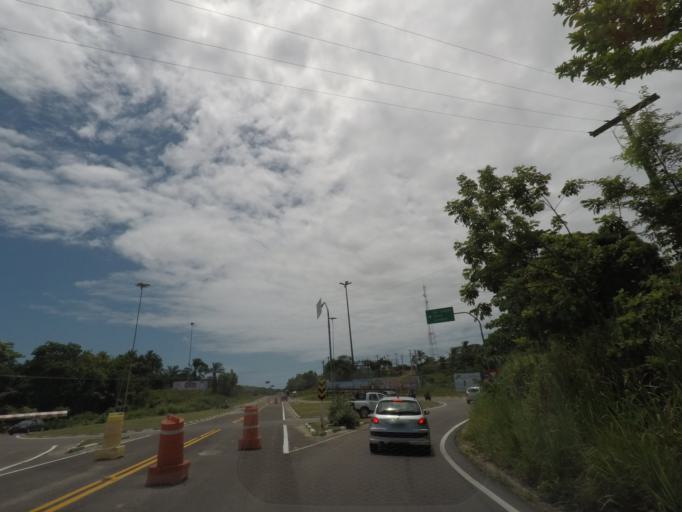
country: BR
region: Bahia
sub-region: Itaparica
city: Itaparica
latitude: -12.9495
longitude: -38.6321
